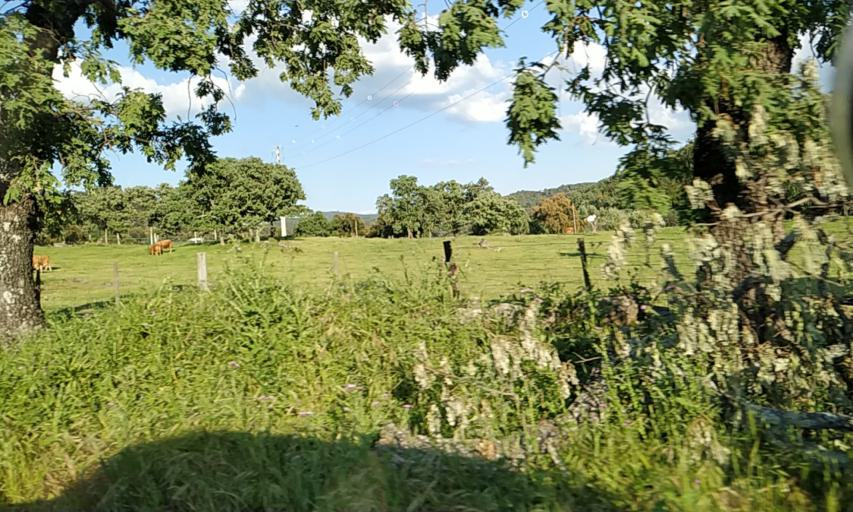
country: PT
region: Portalegre
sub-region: Portalegre
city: Portalegre
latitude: 39.3272
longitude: -7.4333
